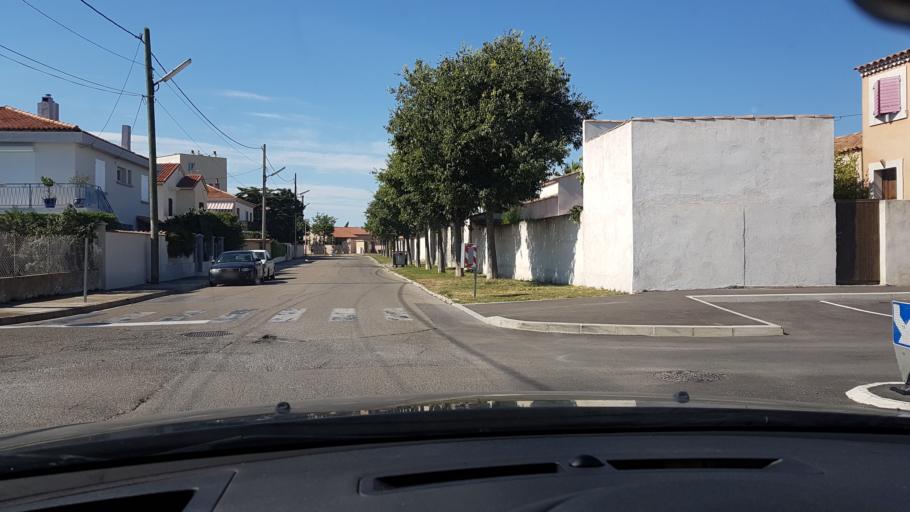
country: FR
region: Provence-Alpes-Cote d'Azur
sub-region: Departement des Bouches-du-Rhone
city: Port-Saint-Louis-du-Rhone
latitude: 43.3891
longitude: 4.8139
